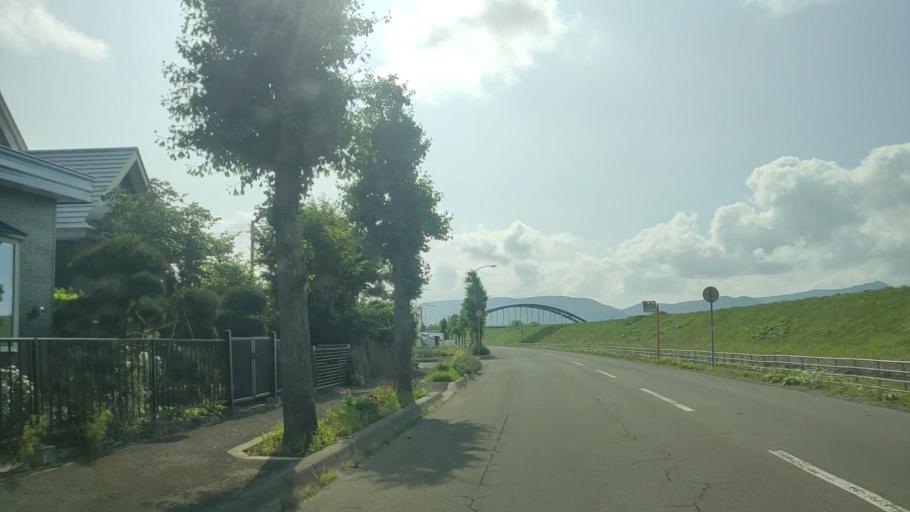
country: JP
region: Hokkaido
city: Shimo-furano
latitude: 43.3403
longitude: 142.3804
